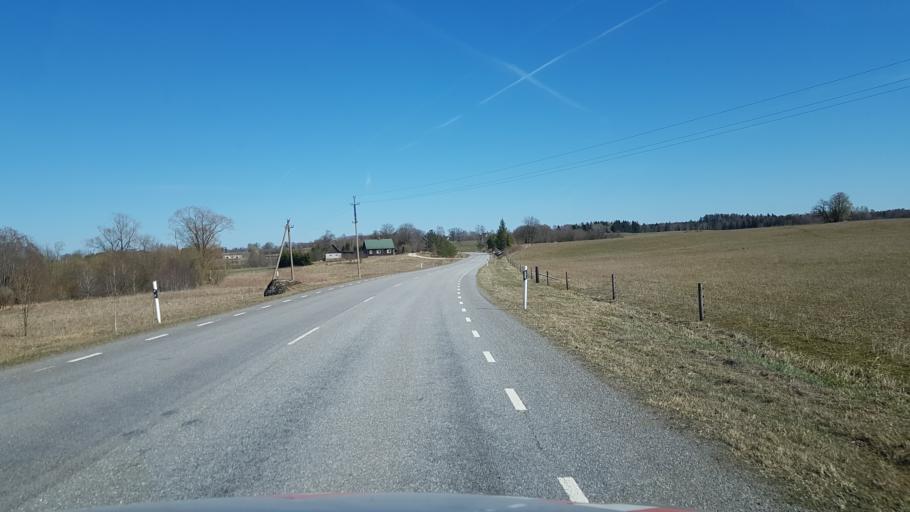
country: EE
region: Laeaene-Virumaa
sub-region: Vinni vald
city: Vinni
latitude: 59.3178
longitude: 26.4743
